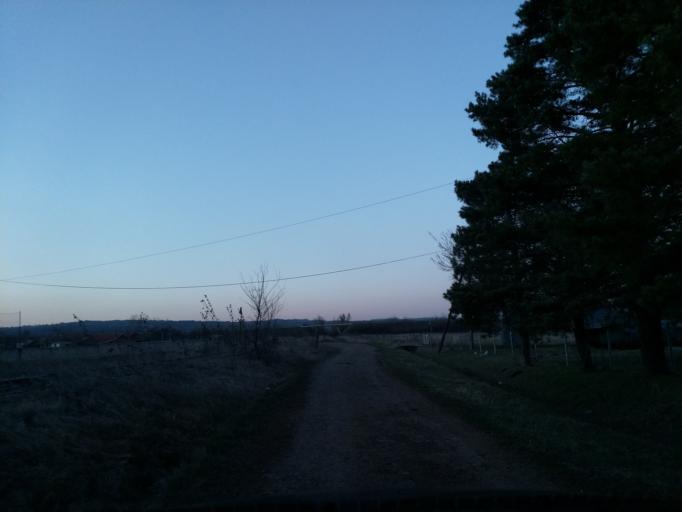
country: RS
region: Central Serbia
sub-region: Pomoravski Okrug
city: Paracin
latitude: 43.8658
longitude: 21.4808
